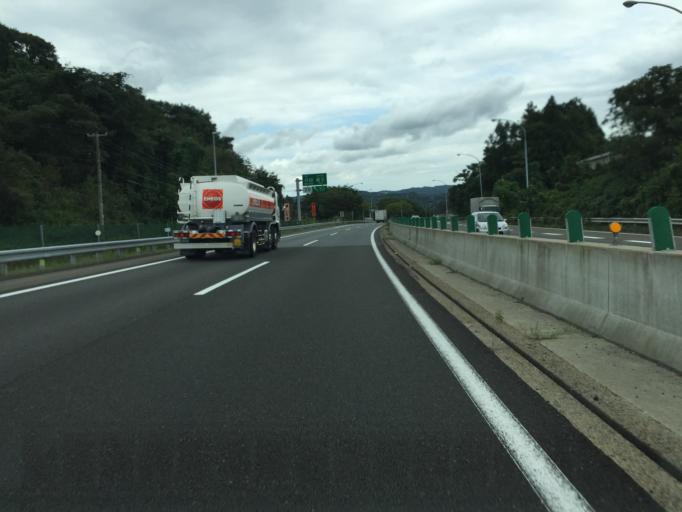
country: JP
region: Miyagi
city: Okawara
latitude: 38.1200
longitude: 140.7083
